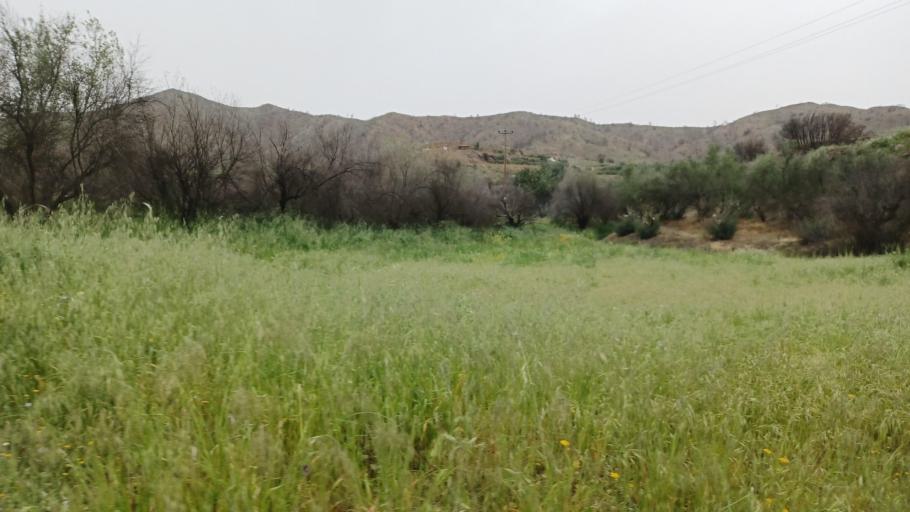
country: CY
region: Limassol
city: Parekklisha
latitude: 34.8474
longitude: 33.1456
